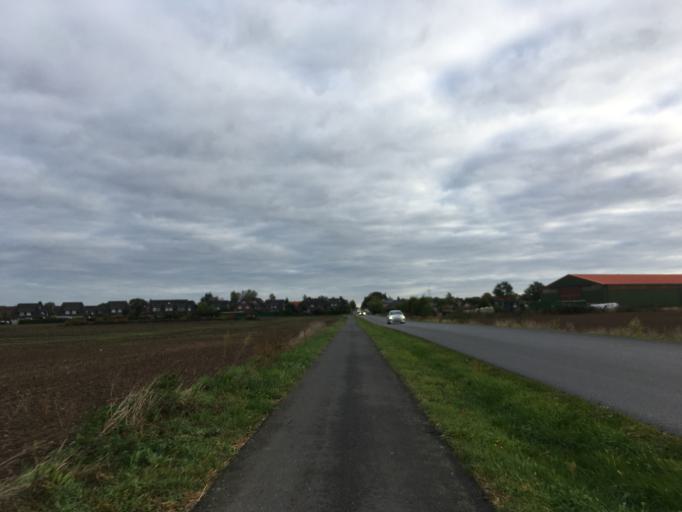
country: DE
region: Berlin
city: Falkenberg
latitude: 52.5954
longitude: 13.5503
